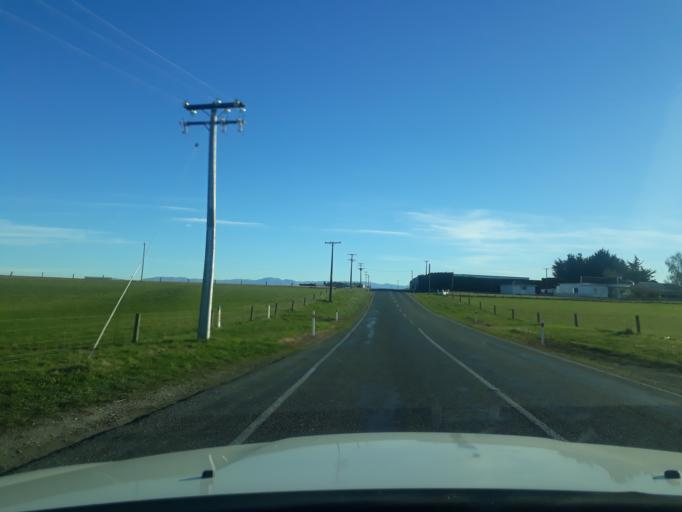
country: NZ
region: Canterbury
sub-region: Timaru District
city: Timaru
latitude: -44.3361
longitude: 171.2235
